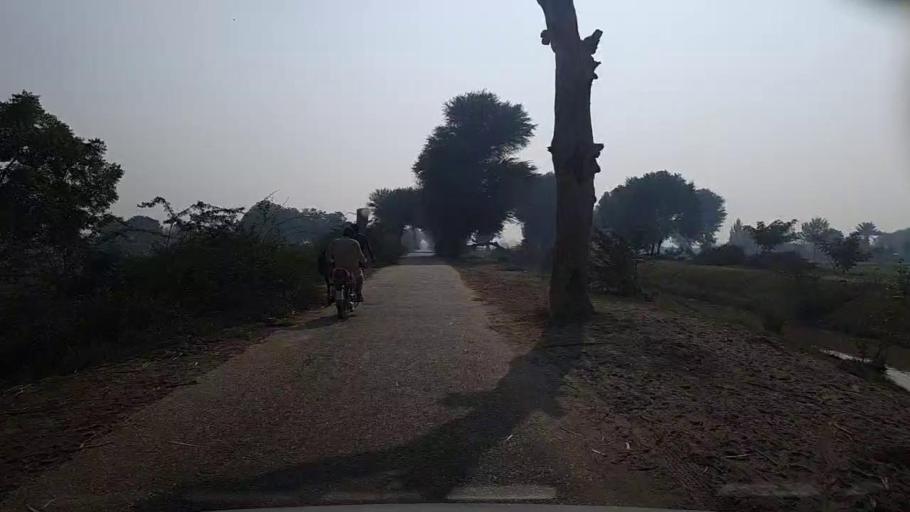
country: PK
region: Sindh
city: Setharja Old
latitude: 27.1141
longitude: 68.5093
